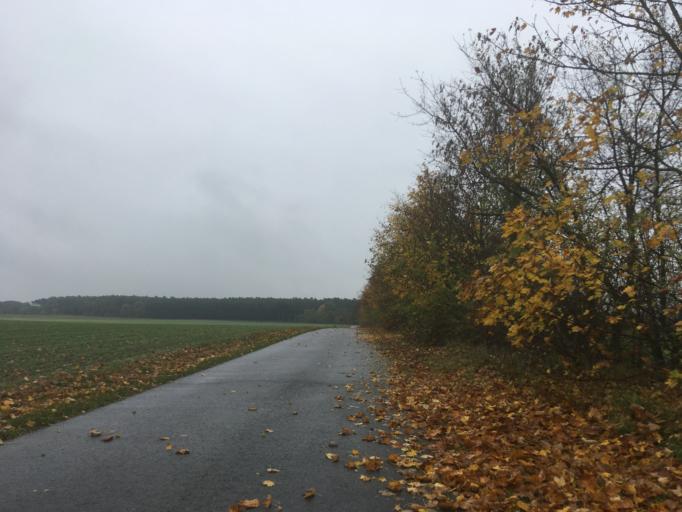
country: DE
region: Brandenburg
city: Neu Zauche
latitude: 52.0262
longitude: 14.0970
